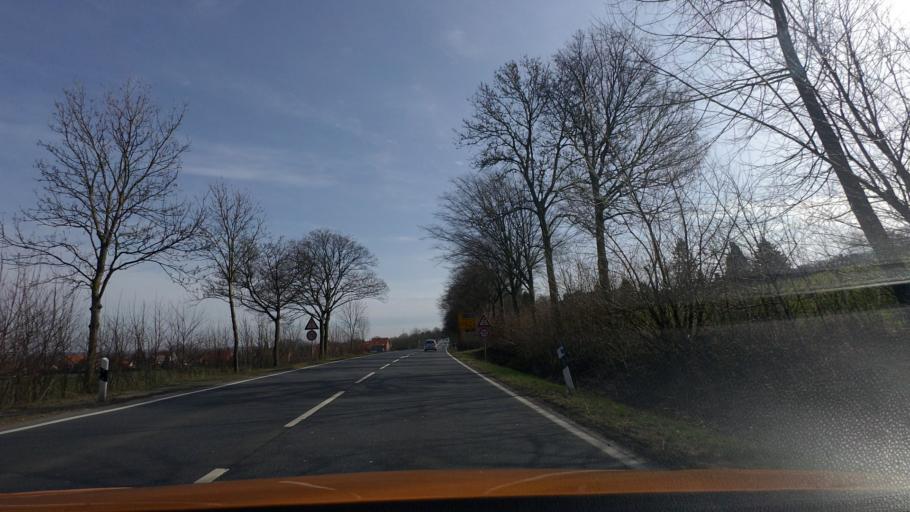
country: DE
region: Lower Saxony
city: Beckedorf
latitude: 52.3396
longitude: 9.3085
